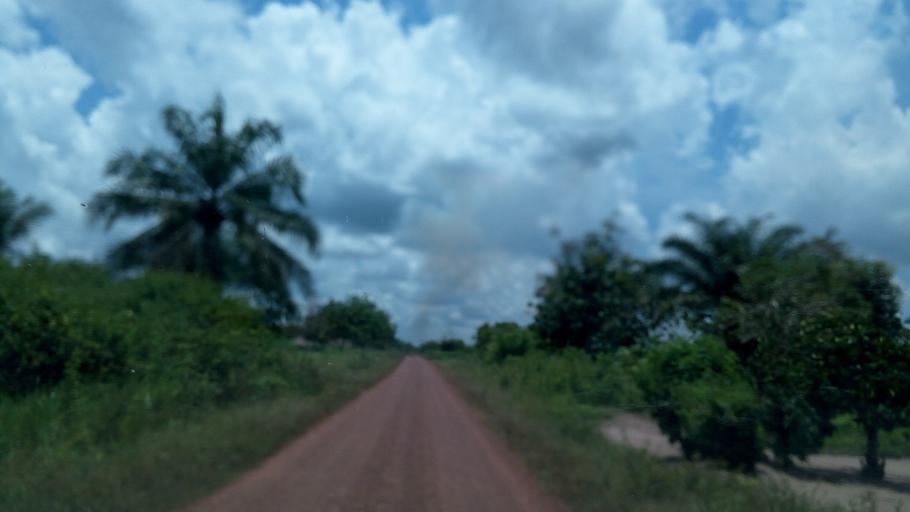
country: CD
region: Equateur
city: Libenge
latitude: 3.7755
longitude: 18.9759
